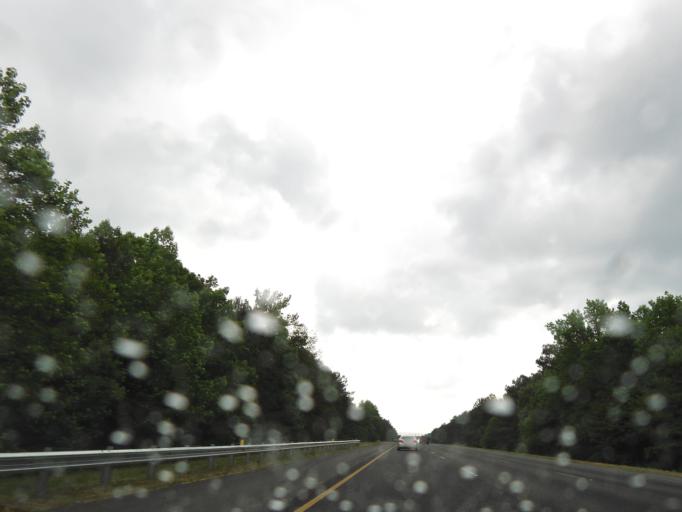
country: US
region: Georgia
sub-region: Carroll County
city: Villa Rica
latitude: 33.7230
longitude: -84.8746
